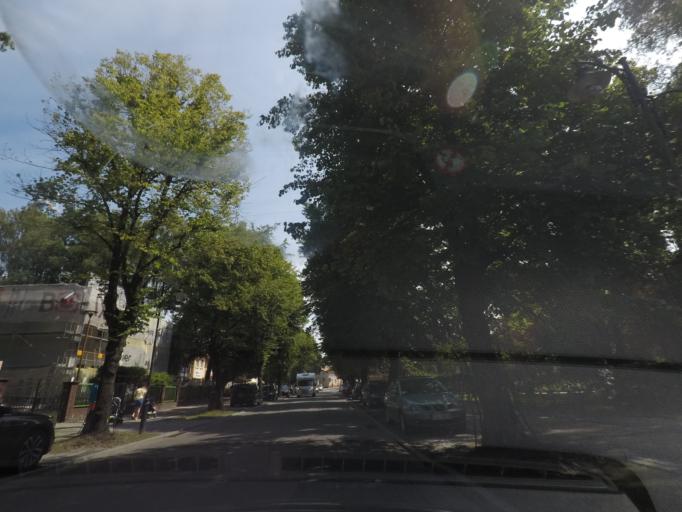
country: PL
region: Pomeranian Voivodeship
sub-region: Powiat slupski
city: Ustka
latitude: 54.5814
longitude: 16.8601
